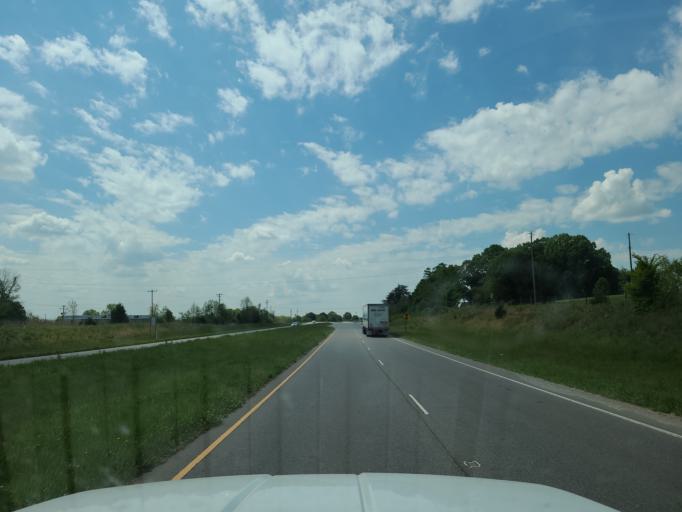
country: US
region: North Carolina
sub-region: Gaston County
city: Cherryville
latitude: 35.4207
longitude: -81.3159
